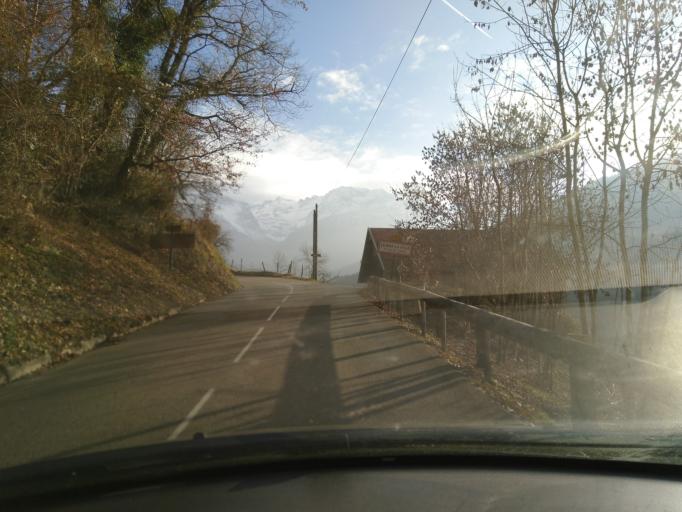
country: FR
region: Rhone-Alpes
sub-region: Departement de l'Isere
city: Villard-Bonnot
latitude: 45.2373
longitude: 5.9190
